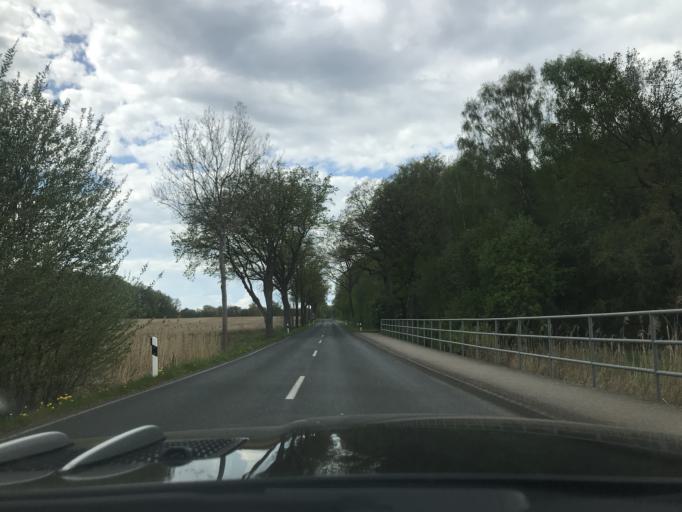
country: DE
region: Schleswig-Holstein
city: Gross Gronau
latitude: 53.7844
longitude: 10.7634
